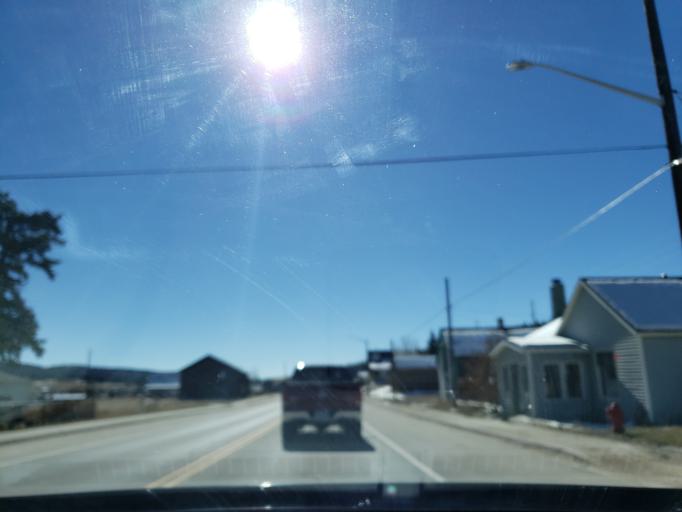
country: US
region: Colorado
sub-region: Park County
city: Fairplay
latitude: 39.2862
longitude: -106.0644
